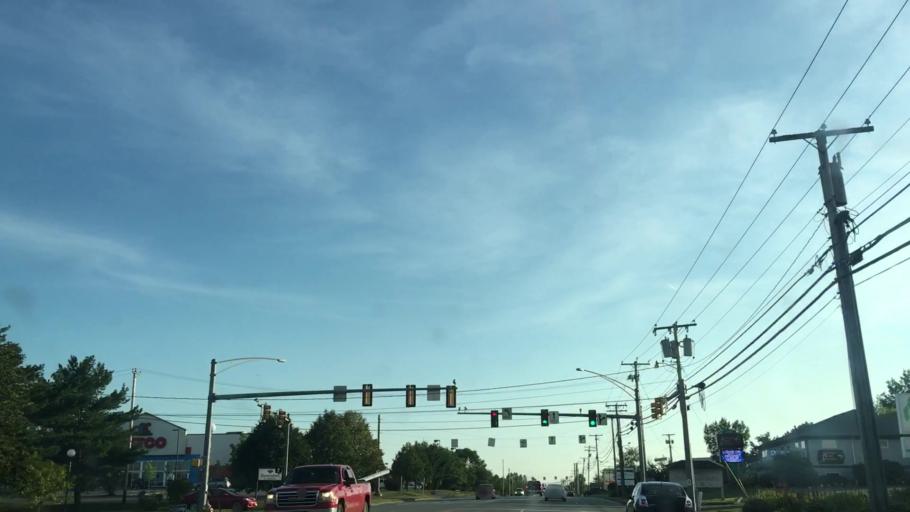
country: US
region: Maine
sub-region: Penobscot County
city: Brewer
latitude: 44.8361
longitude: -68.7487
